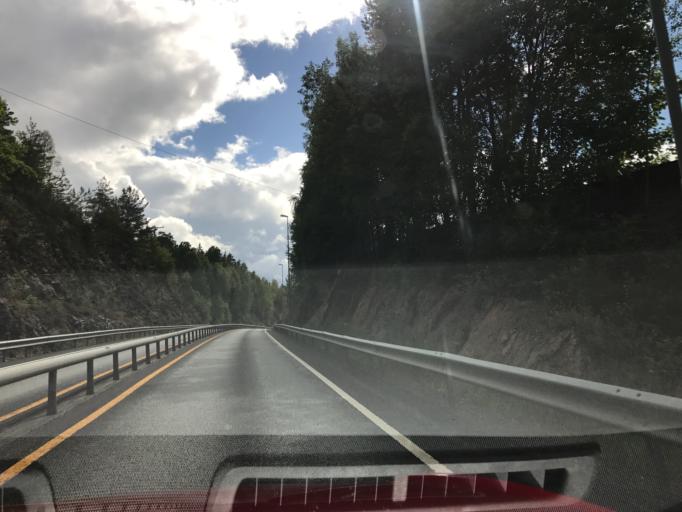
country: NO
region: Aust-Agder
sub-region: Gjerstad
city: Gjerstad
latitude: 58.8415
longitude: 9.1016
